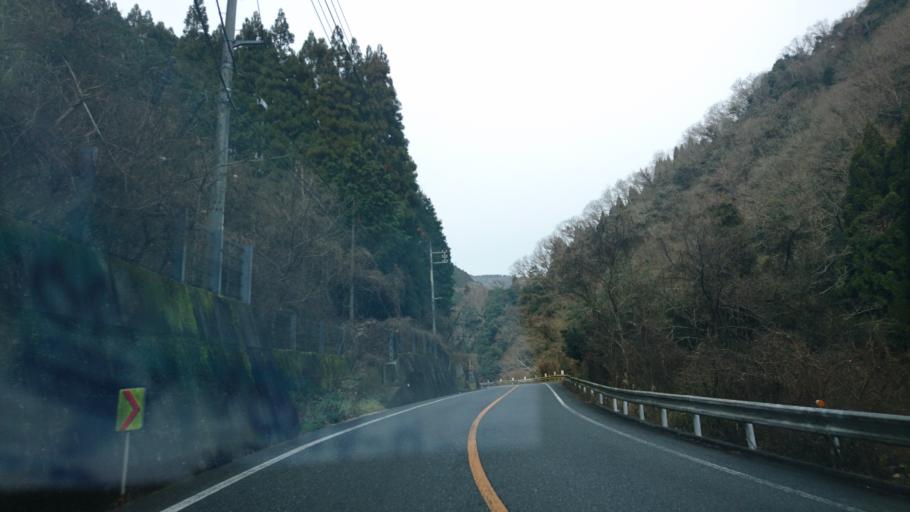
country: JP
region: Okayama
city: Takahashi
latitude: 34.8196
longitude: 133.6345
